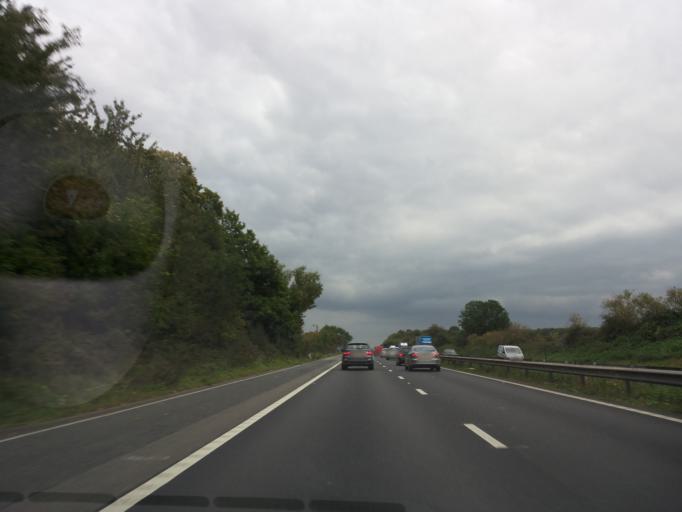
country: GB
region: England
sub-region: Kent
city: Newington
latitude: 51.3347
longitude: 0.6500
